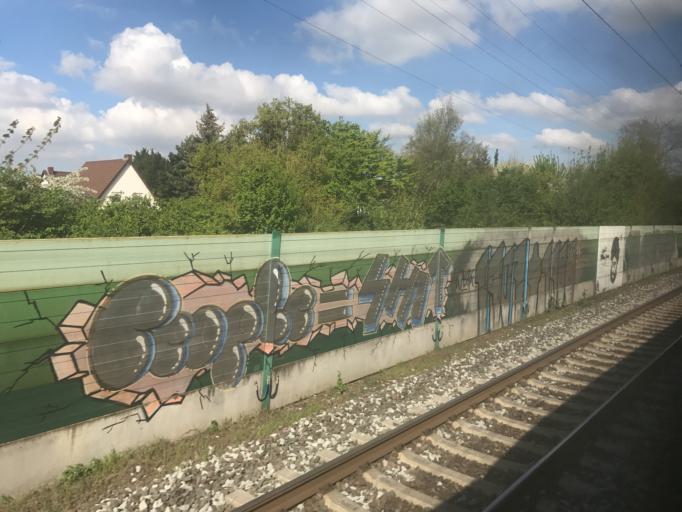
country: DE
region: Rheinland-Pfalz
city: Worms
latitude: 49.6546
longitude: 8.3522
